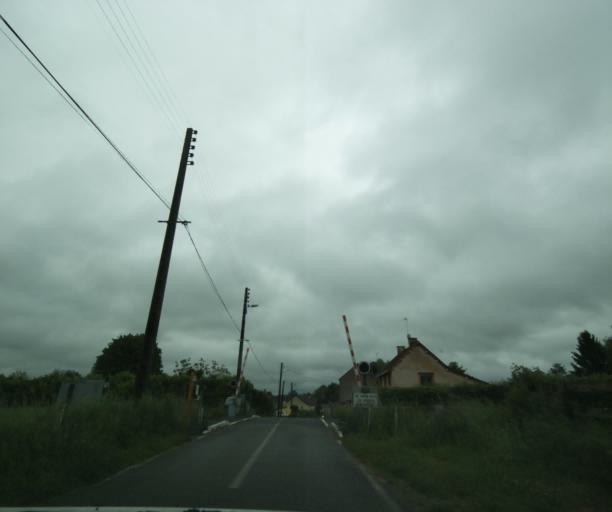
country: FR
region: Bourgogne
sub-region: Departement de Saone-et-Loire
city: Palinges
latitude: 46.5671
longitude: 4.2140
